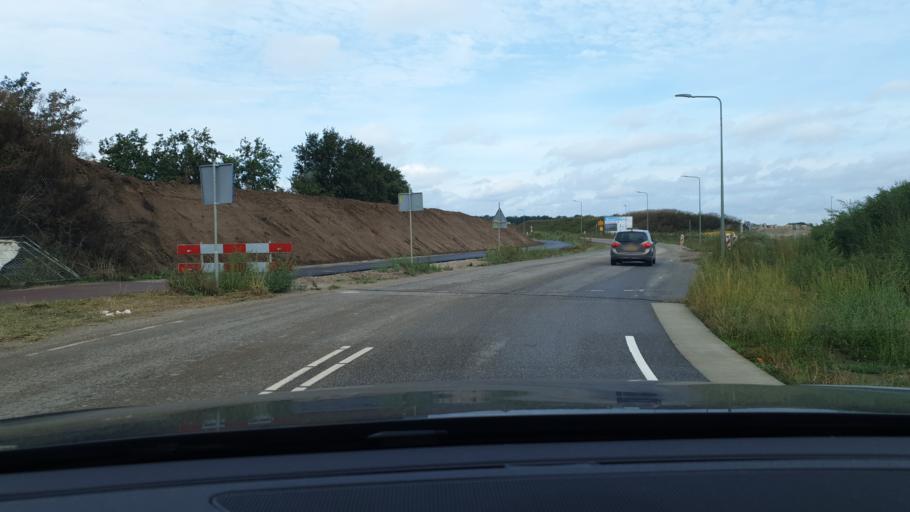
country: NL
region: Limburg
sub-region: Gemeente Bergen
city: Wellerlooi
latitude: 51.5407
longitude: 6.0703
